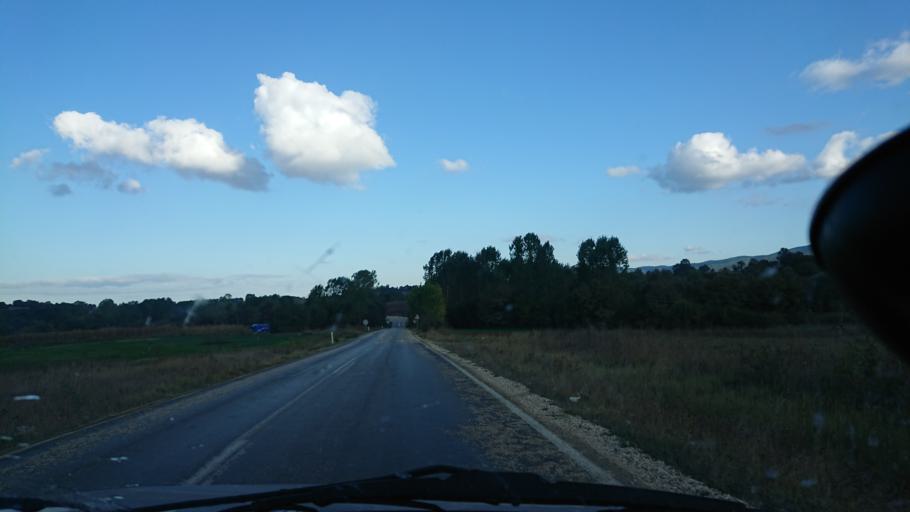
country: TR
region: Bilecik
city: Pazaryeri
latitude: 40.0129
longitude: 29.8527
